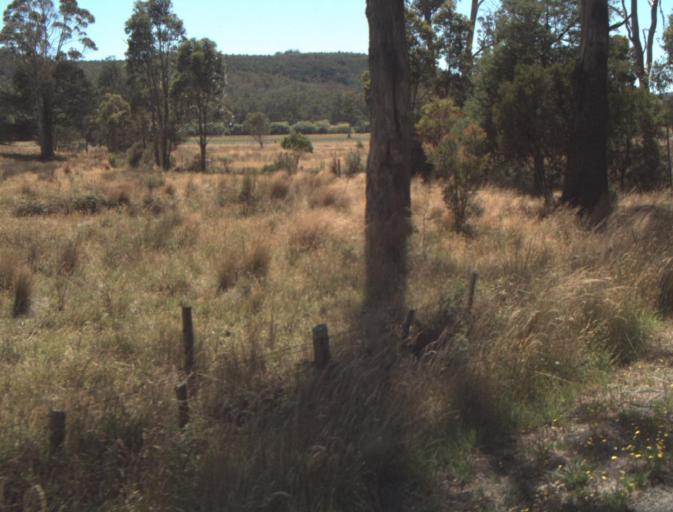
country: AU
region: Tasmania
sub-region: Launceston
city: Newstead
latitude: -41.3317
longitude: 147.3508
